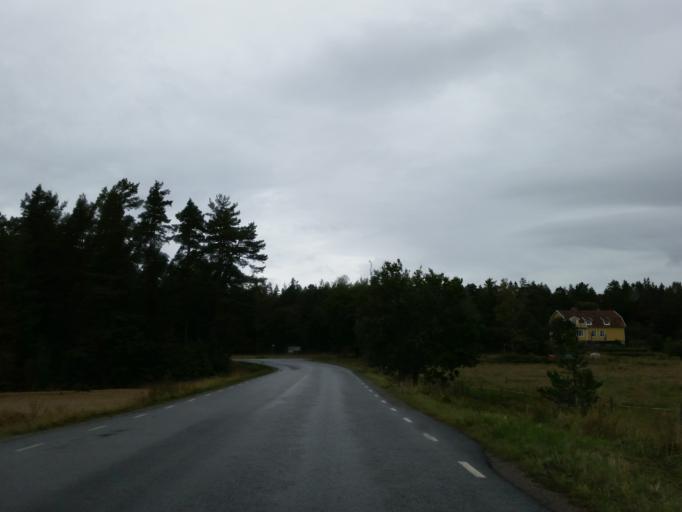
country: SE
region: Uppsala
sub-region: Habo Kommun
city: Balsta
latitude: 59.6532
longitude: 17.4580
